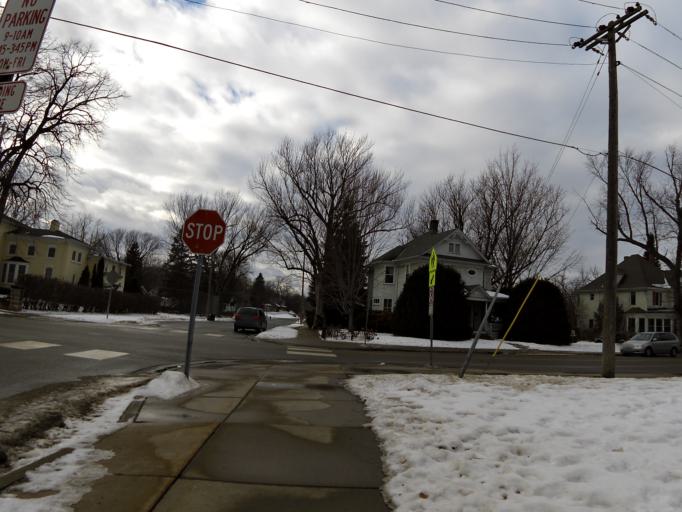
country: US
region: Minnesota
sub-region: Washington County
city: Stillwater
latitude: 45.0501
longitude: -92.8061
